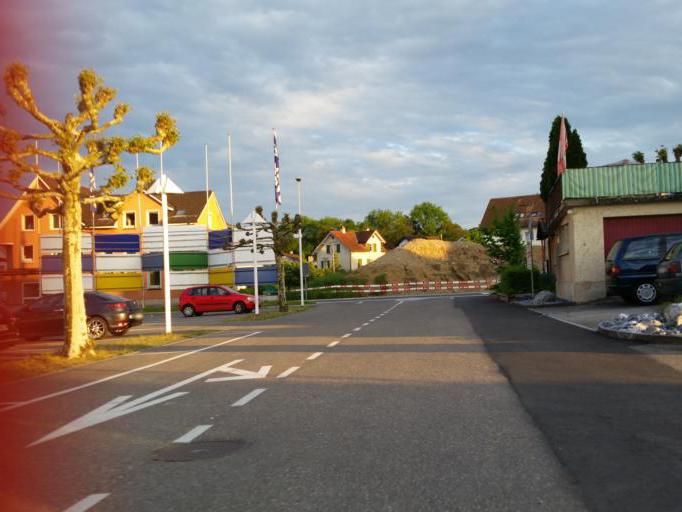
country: CH
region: Thurgau
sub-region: Arbon District
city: Amriswil
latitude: 47.5457
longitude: 9.2933
